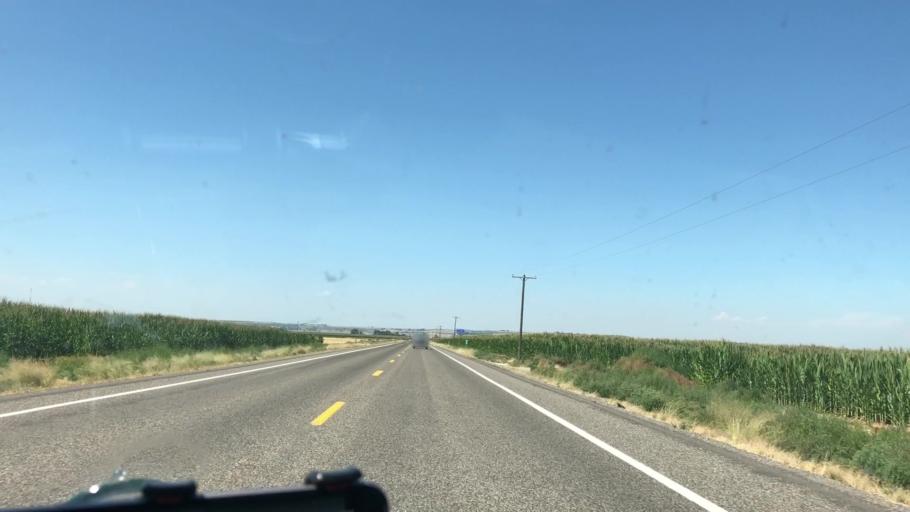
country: US
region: Idaho
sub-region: Owyhee County
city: Marsing
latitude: 43.5258
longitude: -116.8516
